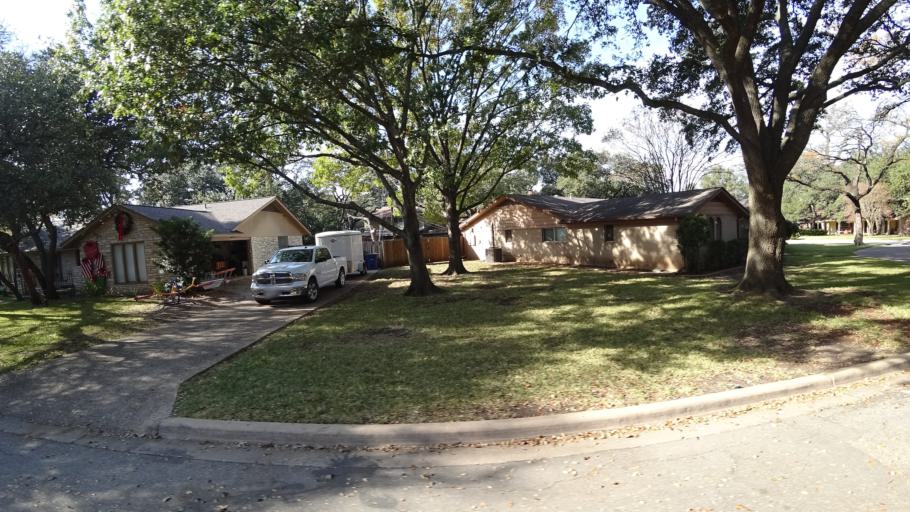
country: US
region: Texas
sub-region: Williamson County
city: Jollyville
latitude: 30.3800
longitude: -97.7530
